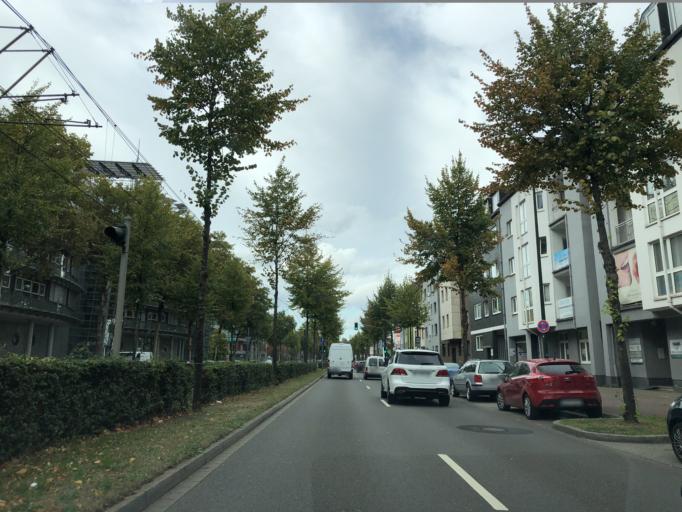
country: DE
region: North Rhine-Westphalia
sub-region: Regierungsbezirk Dusseldorf
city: Dusseldorf
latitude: 51.1949
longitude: 6.8137
